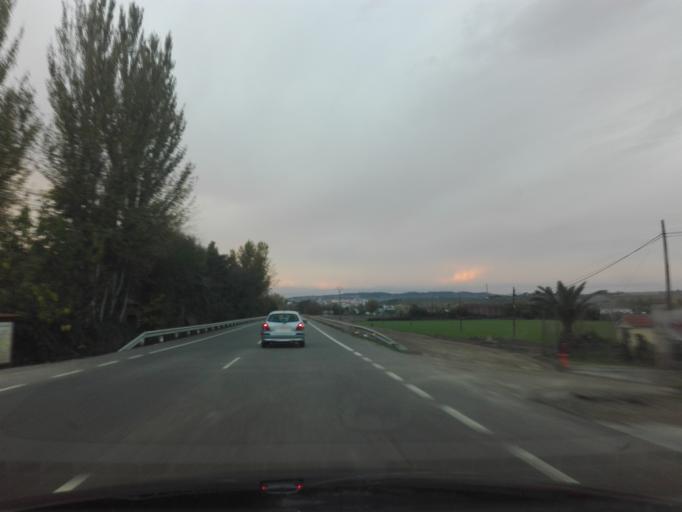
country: ES
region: Extremadura
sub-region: Provincia de Caceres
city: Coria
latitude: 39.9689
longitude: -6.5212
